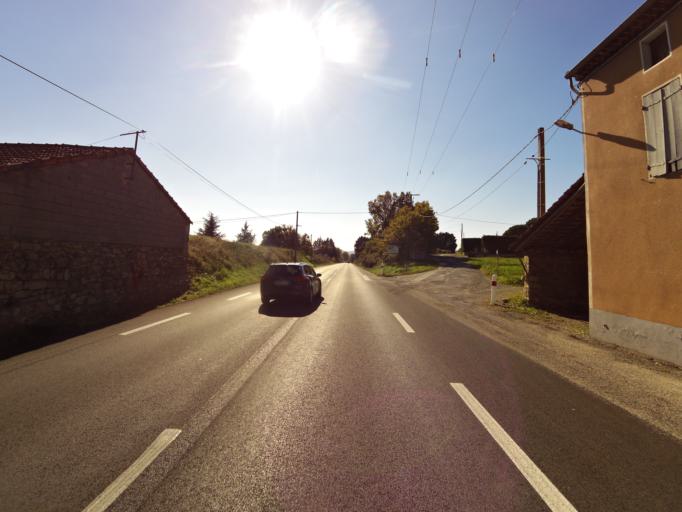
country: FR
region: Rhone-Alpes
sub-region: Departement de l'Ardeche
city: Saint-Privat
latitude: 44.6353
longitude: 4.4237
